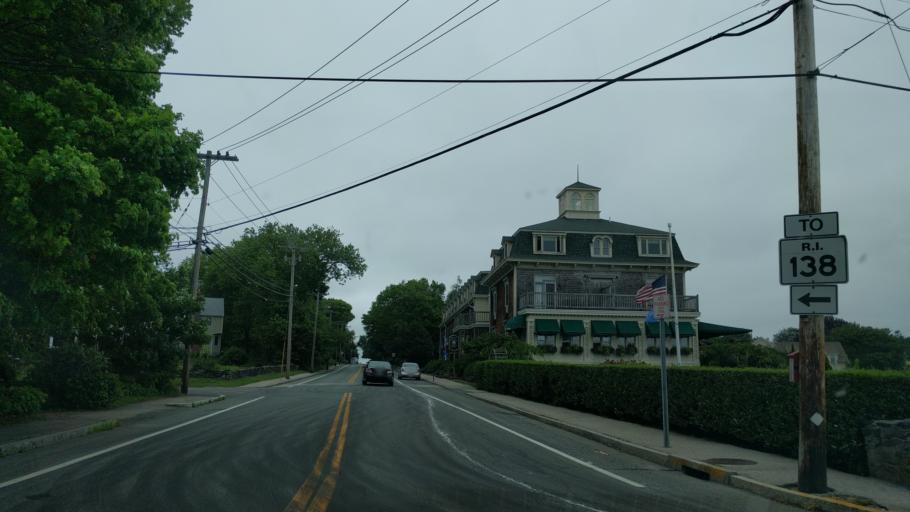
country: US
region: Rhode Island
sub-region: Newport County
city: Jamestown
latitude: 41.5010
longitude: -71.3646
